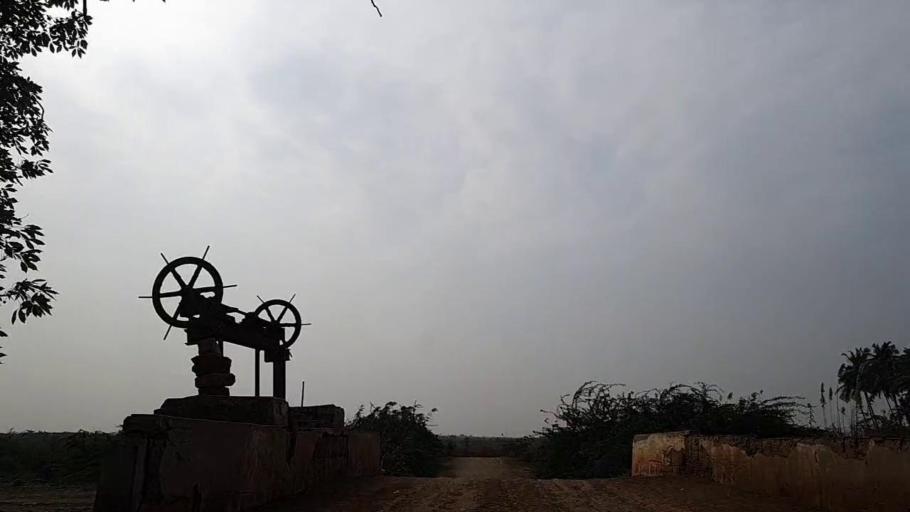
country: PK
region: Sindh
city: Thatta
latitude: 24.7427
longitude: 67.8389
